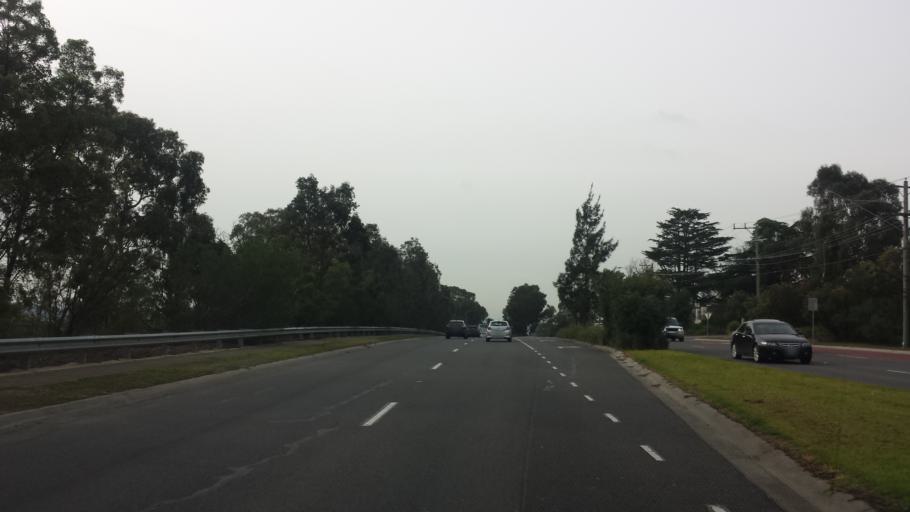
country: AU
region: Victoria
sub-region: Manningham
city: Doncaster
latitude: -37.7763
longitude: 145.1252
